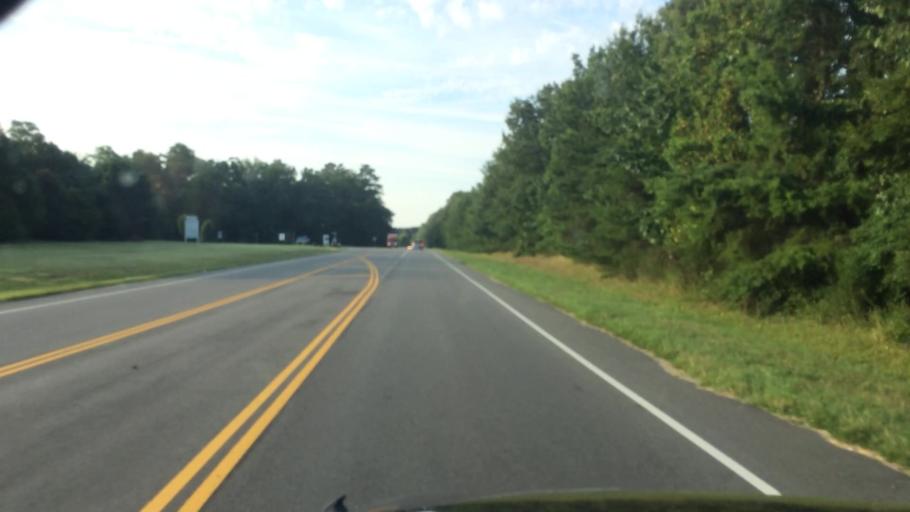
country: US
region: Virginia
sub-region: James City County
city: Williamsburg
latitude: 37.2937
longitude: -76.7232
